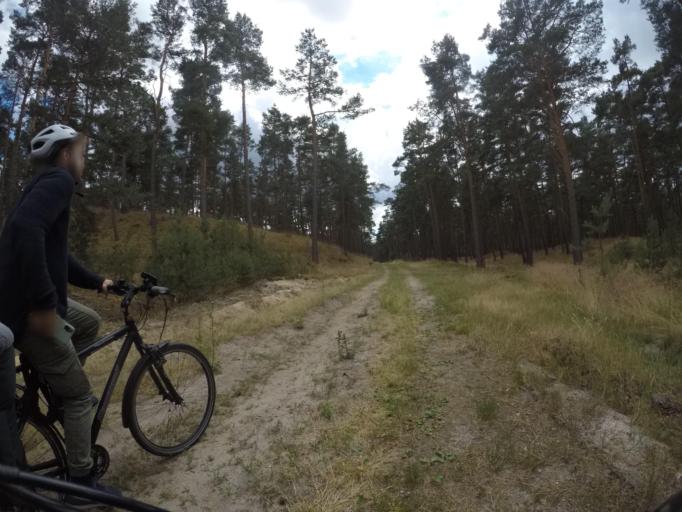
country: DE
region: Lower Saxony
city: Hitzacker
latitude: 53.1884
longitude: 11.0670
